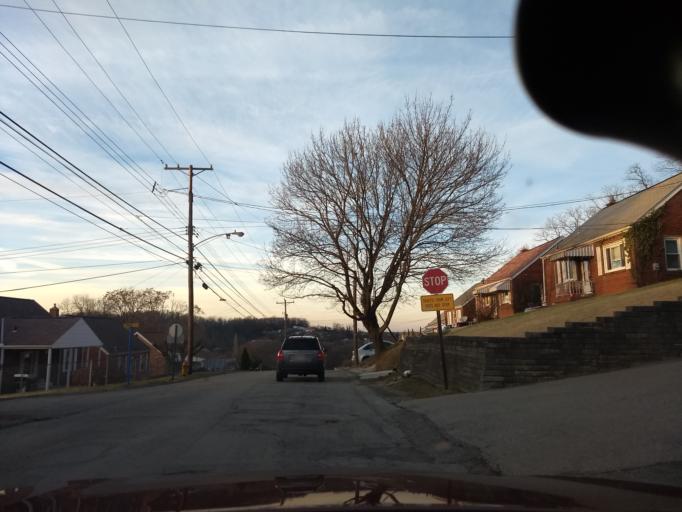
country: US
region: Pennsylvania
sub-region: Allegheny County
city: West Homestead
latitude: 40.3650
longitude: -79.9278
